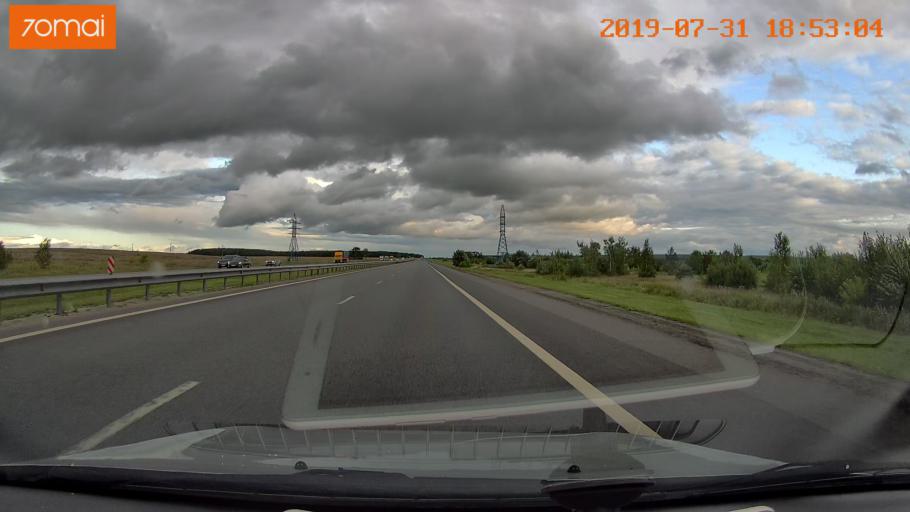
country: RU
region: Moskovskaya
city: Raduzhnyy
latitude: 55.2071
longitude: 38.6454
